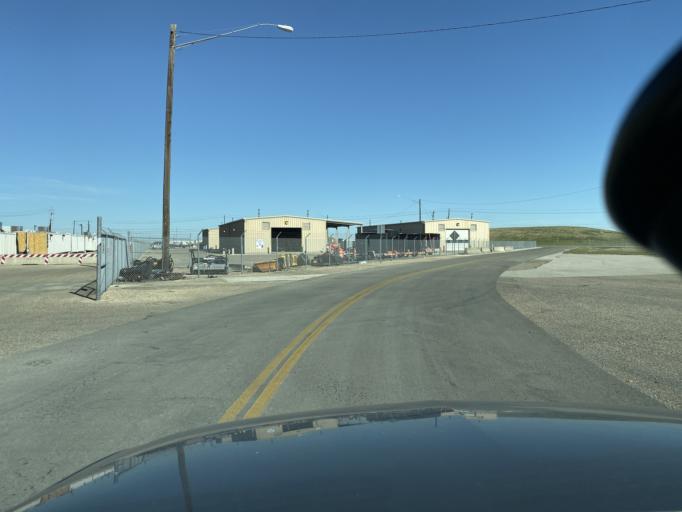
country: US
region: Texas
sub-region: Travis County
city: Hornsby Bend
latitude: 30.1927
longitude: -97.6657
